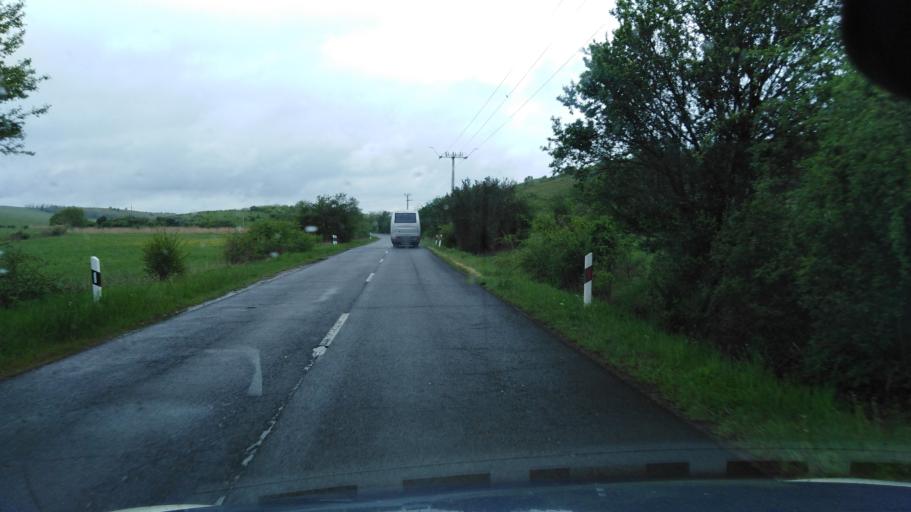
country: HU
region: Nograd
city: Rimoc
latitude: 48.0044
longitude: 19.6148
